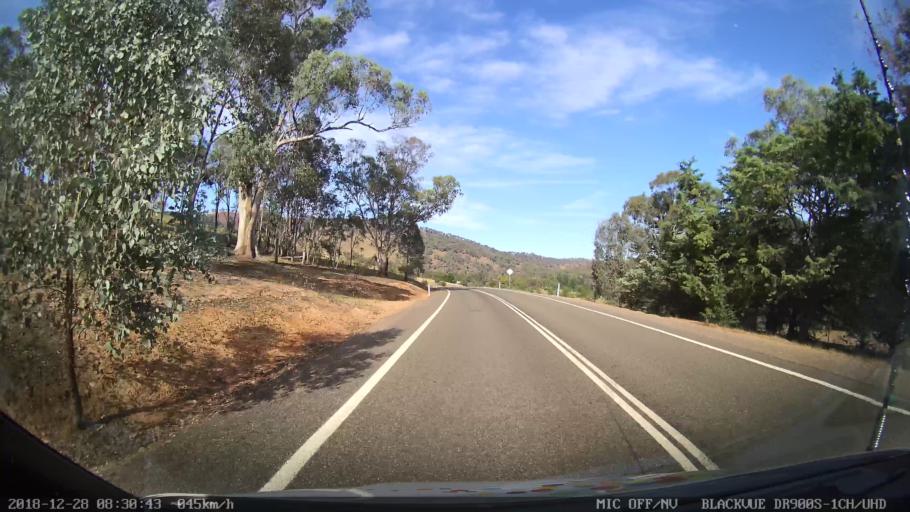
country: AU
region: New South Wales
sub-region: Blayney
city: Blayney
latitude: -33.9570
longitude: 149.3232
